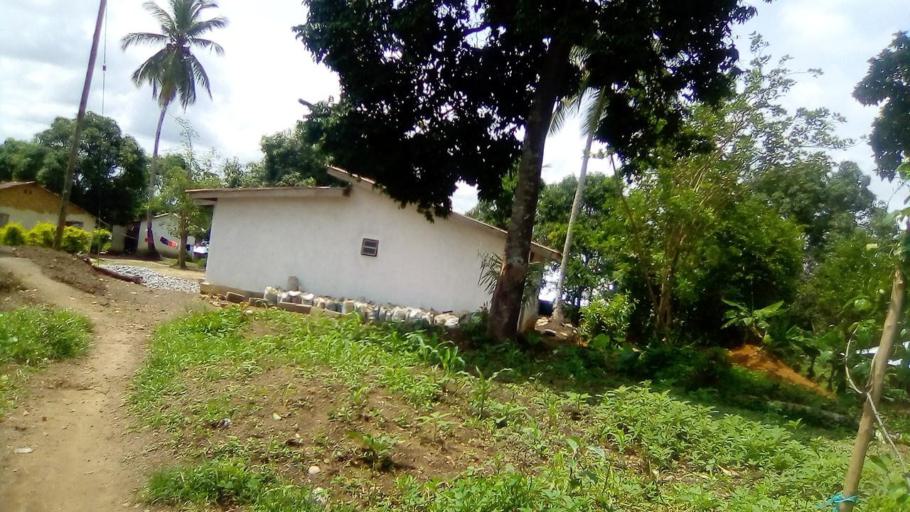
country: SL
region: Southern Province
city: Bo
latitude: 7.9355
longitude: -11.7437
